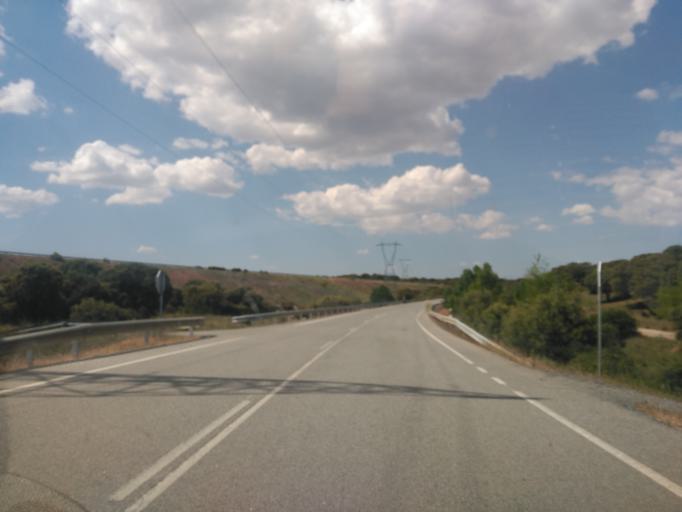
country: ES
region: Castille and Leon
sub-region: Provincia de Salamanca
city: Belena
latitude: 40.7291
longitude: -5.6321
